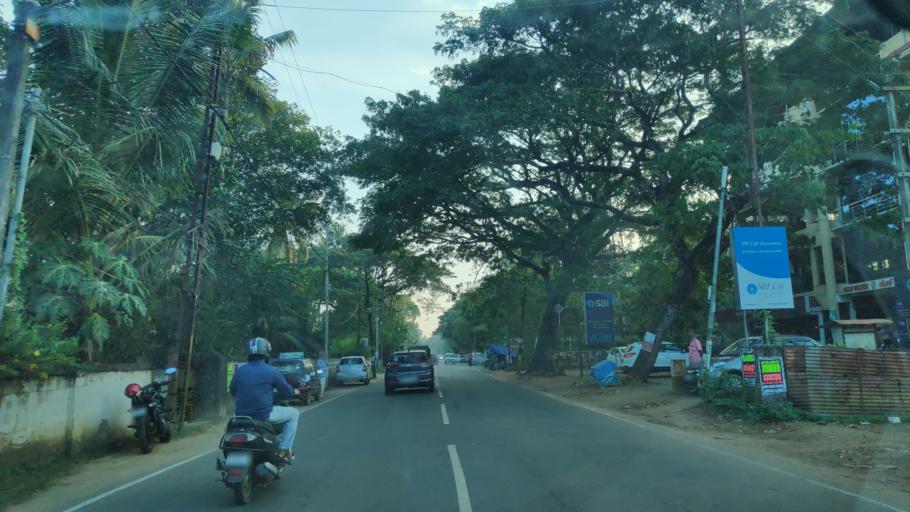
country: IN
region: Kerala
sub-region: Alappuzha
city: Shertallai
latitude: 9.6794
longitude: 76.3412
